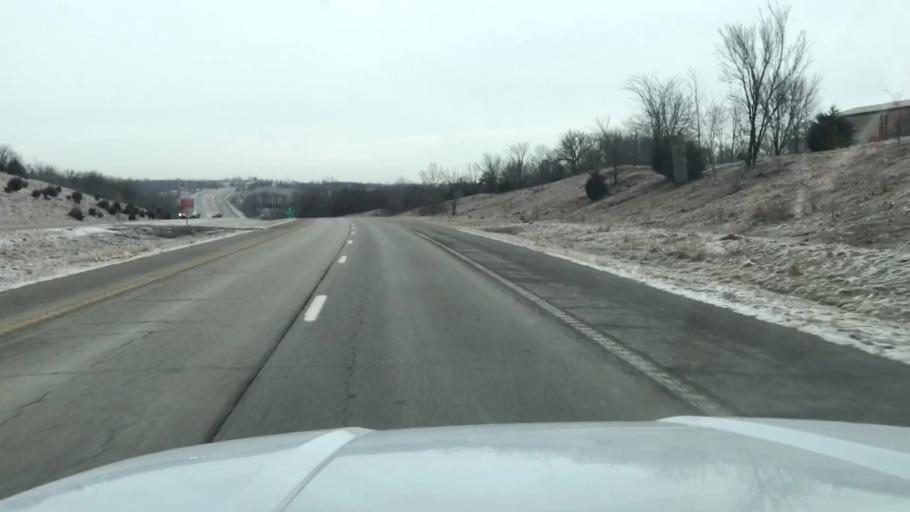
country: US
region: Missouri
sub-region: Andrew County
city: Savannah
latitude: 39.9003
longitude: -94.8571
